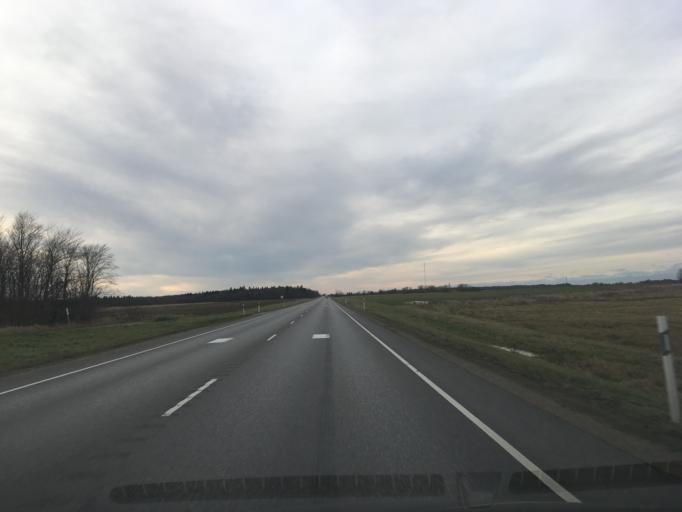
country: EE
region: Ida-Virumaa
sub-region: Kohtla-Jaerve linn
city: Kohtla-Jarve
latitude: 59.4210
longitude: 27.2358
